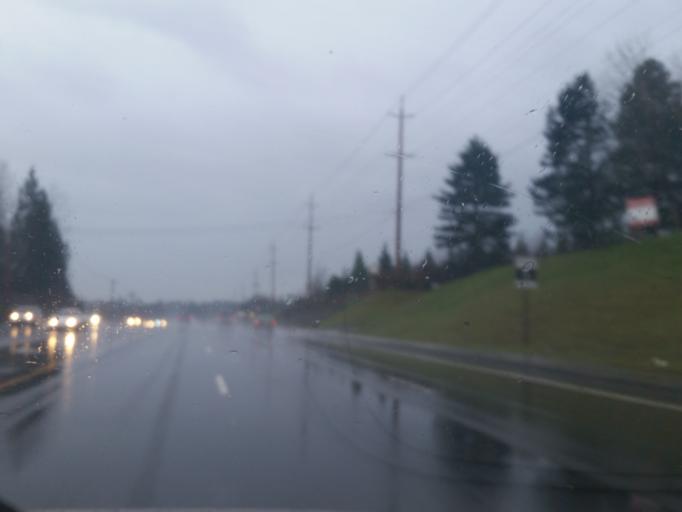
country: US
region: Washington
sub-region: Snohomish County
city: Martha Lake
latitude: 47.8951
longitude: -122.2626
